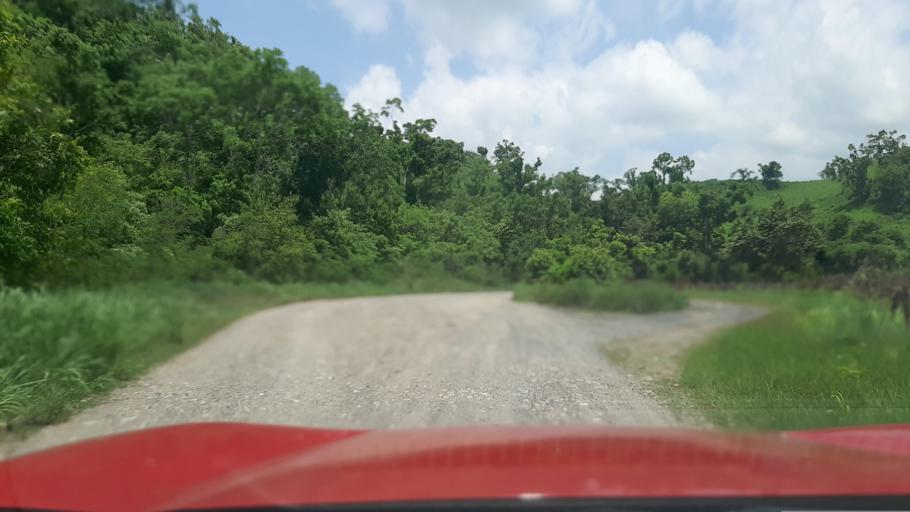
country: MX
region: Veracruz
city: Papantla de Olarte
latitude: 20.4237
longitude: -97.2652
